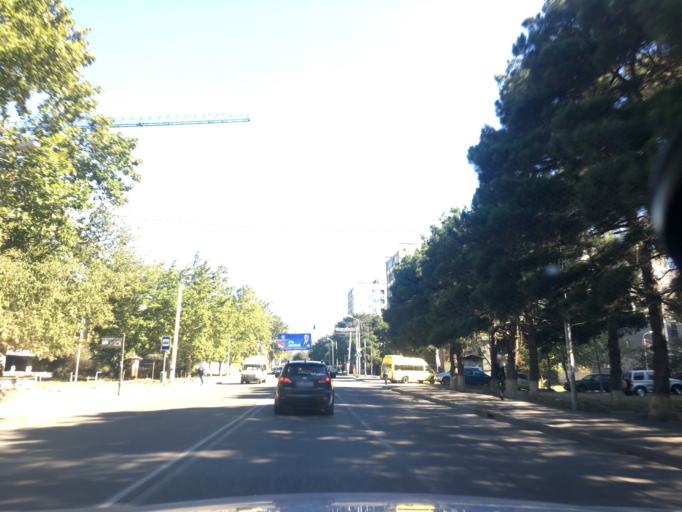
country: GE
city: Zahesi
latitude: 41.7944
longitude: 44.8082
